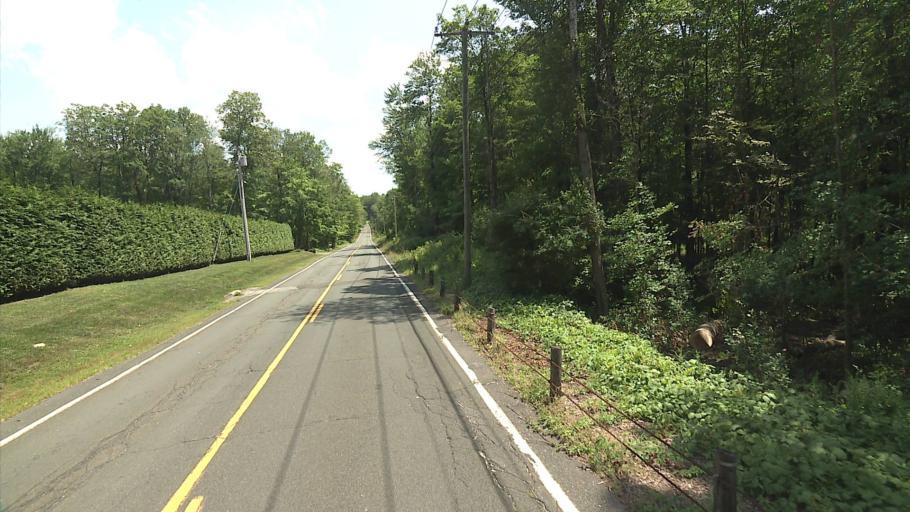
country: US
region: Connecticut
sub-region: Litchfield County
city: Winchester Center
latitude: 41.9889
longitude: -73.1462
